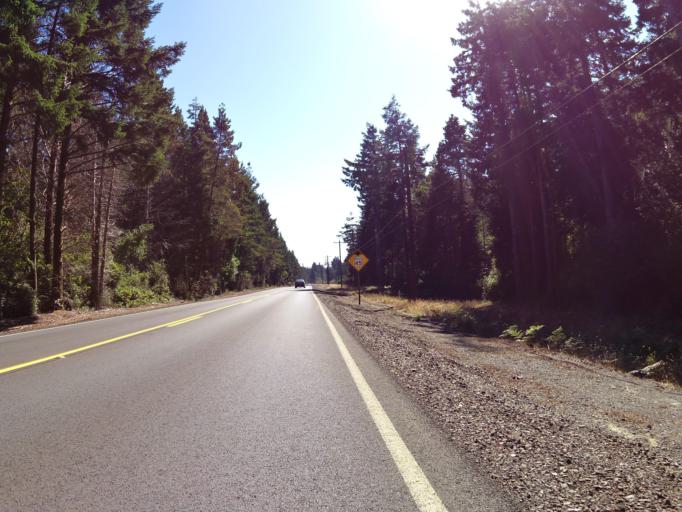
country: US
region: Oregon
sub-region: Coos County
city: Bandon
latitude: 43.1909
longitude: -124.3675
